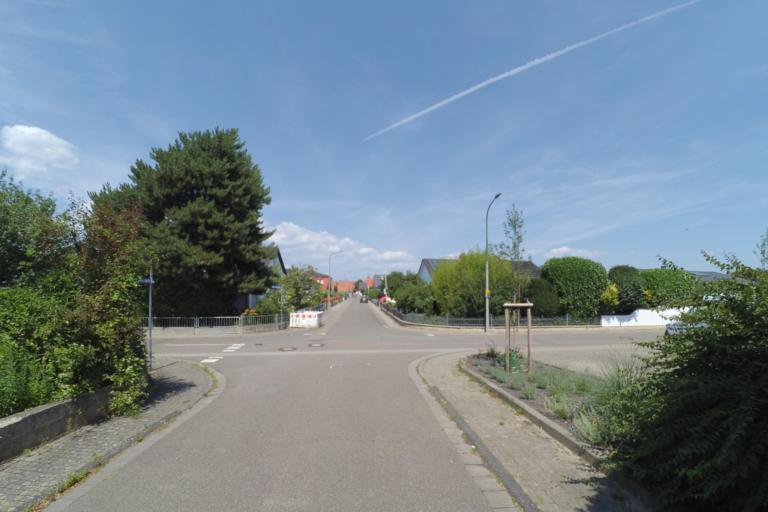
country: DE
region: Rheinland-Pfalz
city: Bornheim
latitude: 49.2196
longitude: 8.1648
